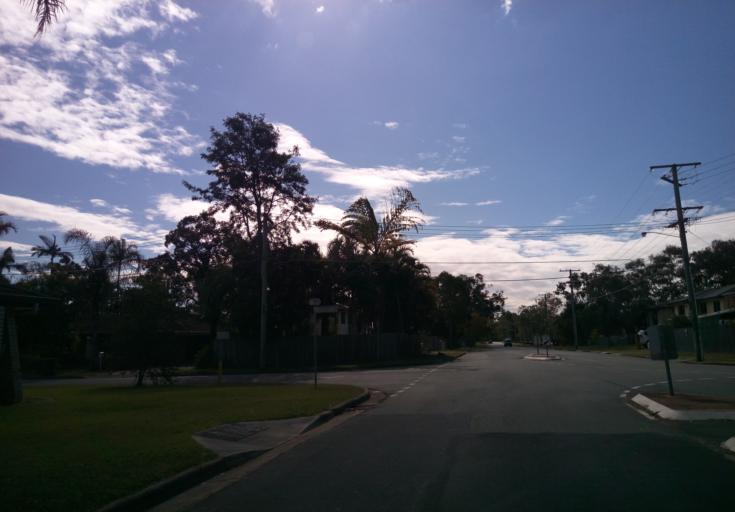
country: AU
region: Queensland
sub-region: Brisbane
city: Manly West
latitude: -27.4899
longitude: 153.2053
